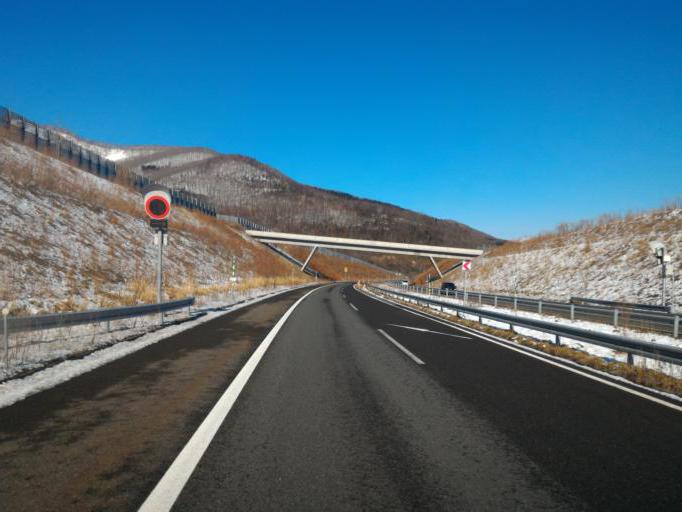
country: JP
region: Hokkaido
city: Otofuke
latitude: 43.0391
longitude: 142.7847
